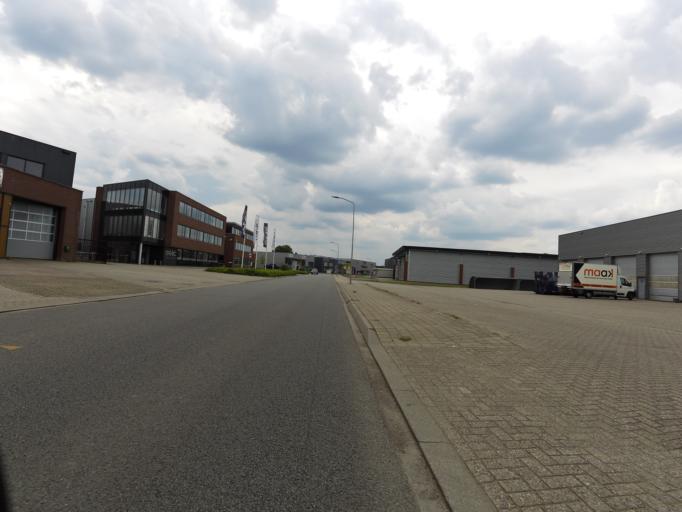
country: NL
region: Gelderland
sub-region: Gemeente Doetinchem
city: Doetinchem
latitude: 51.9467
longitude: 6.2827
